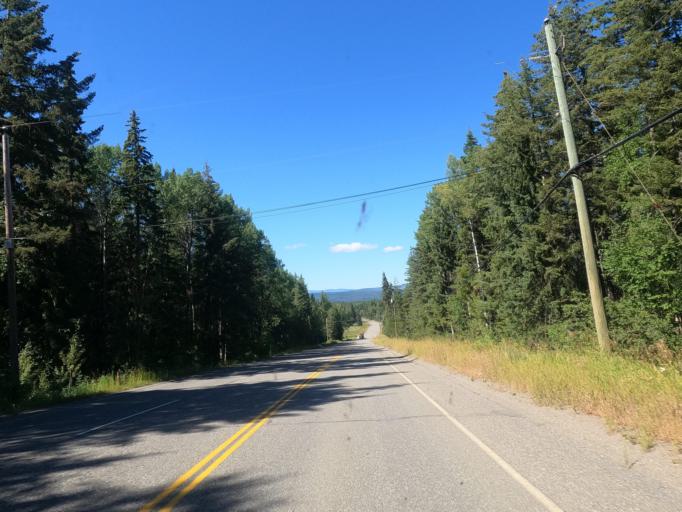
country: CA
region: British Columbia
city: Quesnel
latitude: 53.0238
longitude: -122.4409
